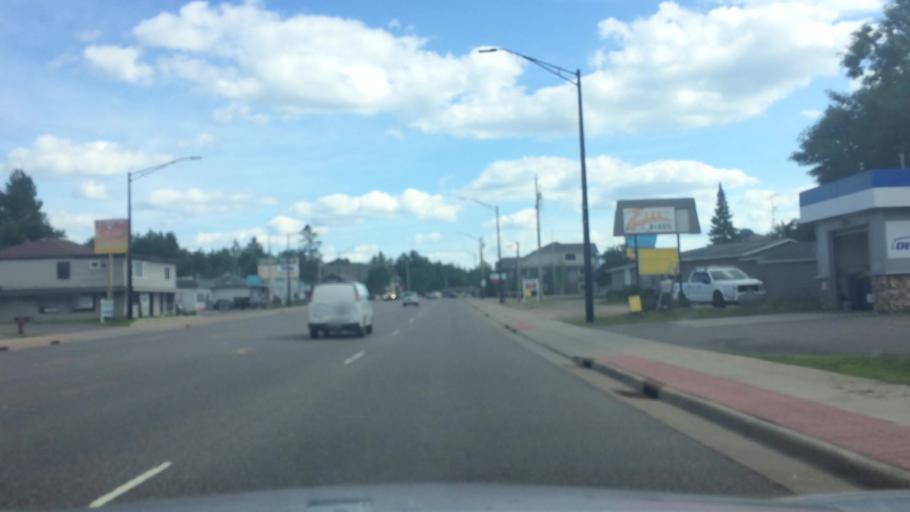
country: US
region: Wisconsin
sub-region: Vilas County
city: Lac du Flambeau
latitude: 45.8828
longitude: -89.7039
